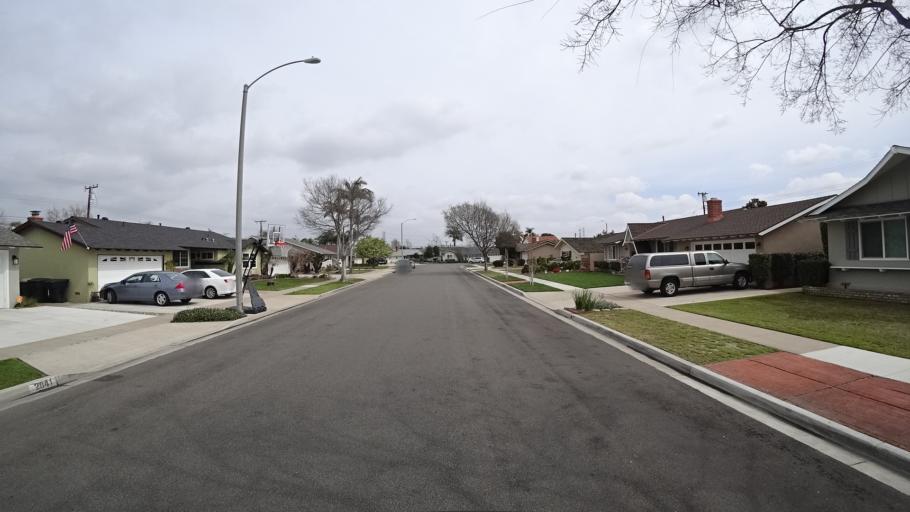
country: US
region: California
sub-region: Orange County
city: Stanton
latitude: 33.8226
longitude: -117.9868
